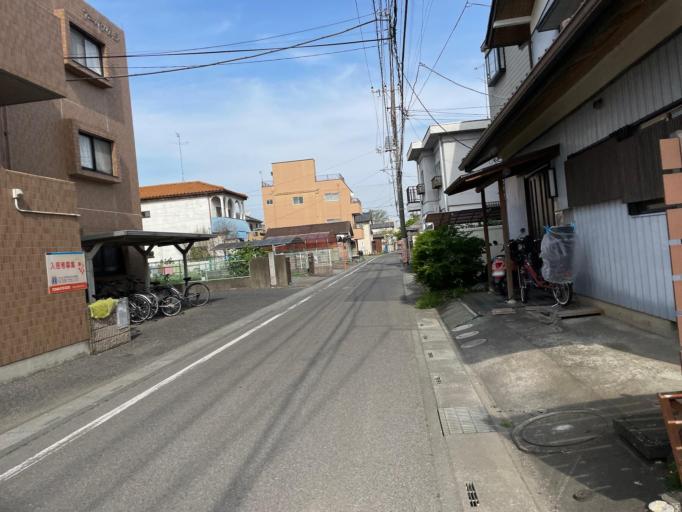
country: JP
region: Saitama
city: Fukayacho
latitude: 36.1944
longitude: 139.2767
